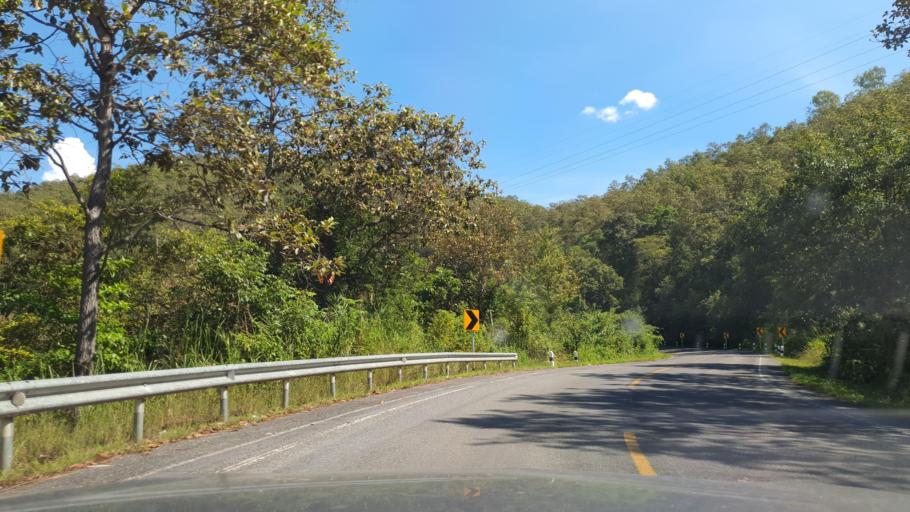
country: TH
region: Chiang Mai
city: Phrao
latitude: 19.3695
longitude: 99.2446
